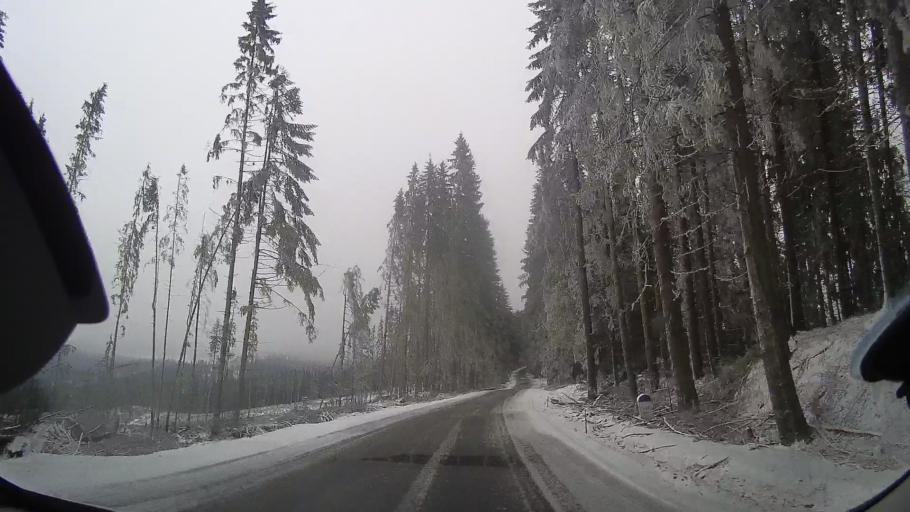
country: RO
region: Cluj
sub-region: Comuna Belis
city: Belis
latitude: 46.6454
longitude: 23.0426
